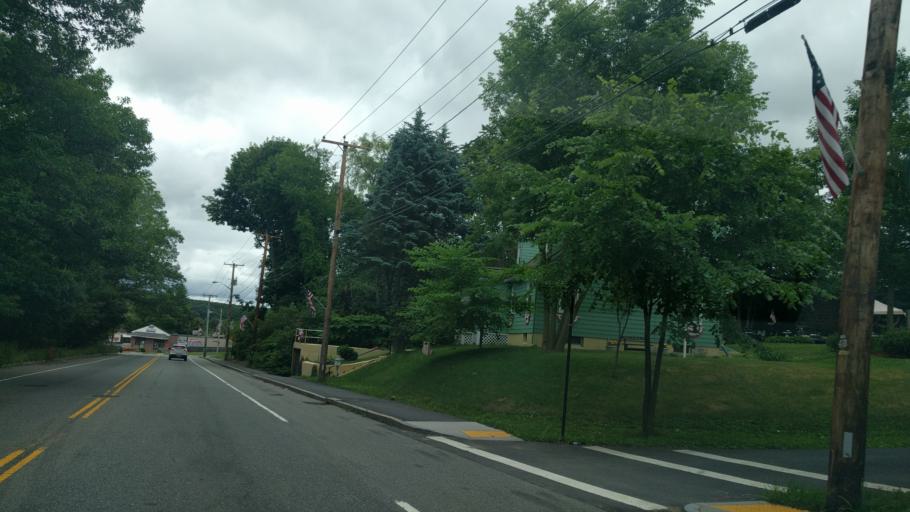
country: US
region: Massachusetts
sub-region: Worcester County
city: Worcester
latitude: 42.2356
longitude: -71.7996
